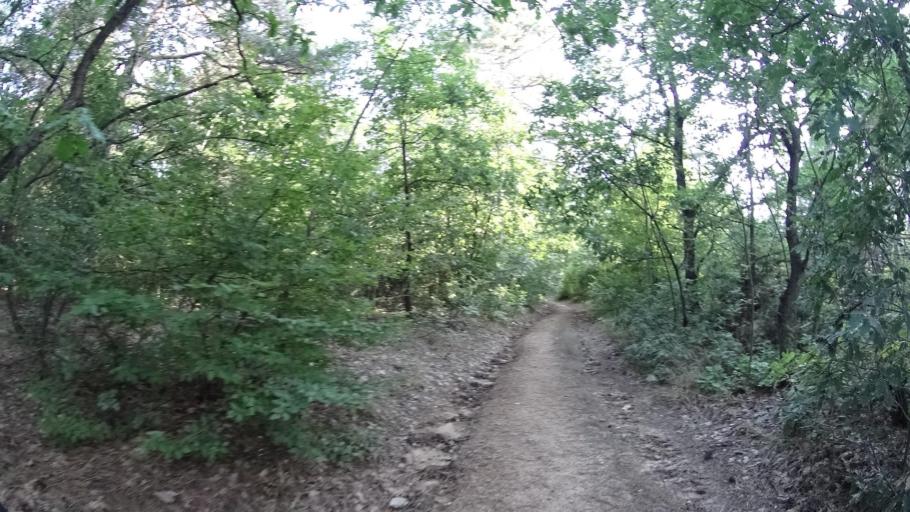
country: BG
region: Plovdiv
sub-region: Obshtina Plovdiv
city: Plovdiv
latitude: 42.0560
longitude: 24.6860
